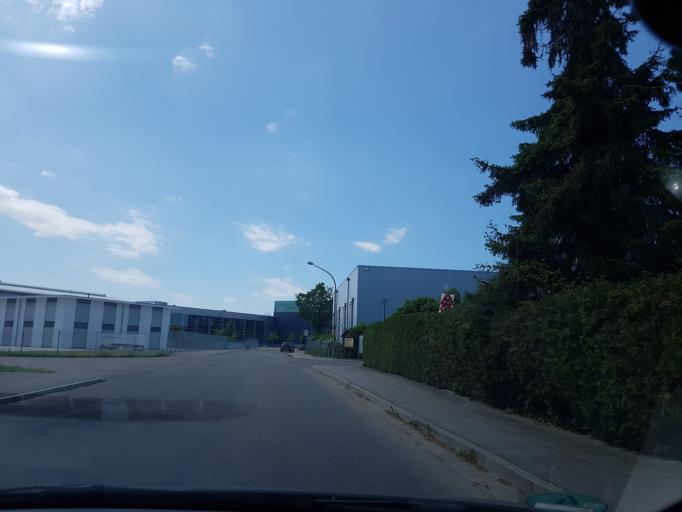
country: DE
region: Bavaria
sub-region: Swabia
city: Nersingen
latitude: 48.4179
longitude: 10.1552
